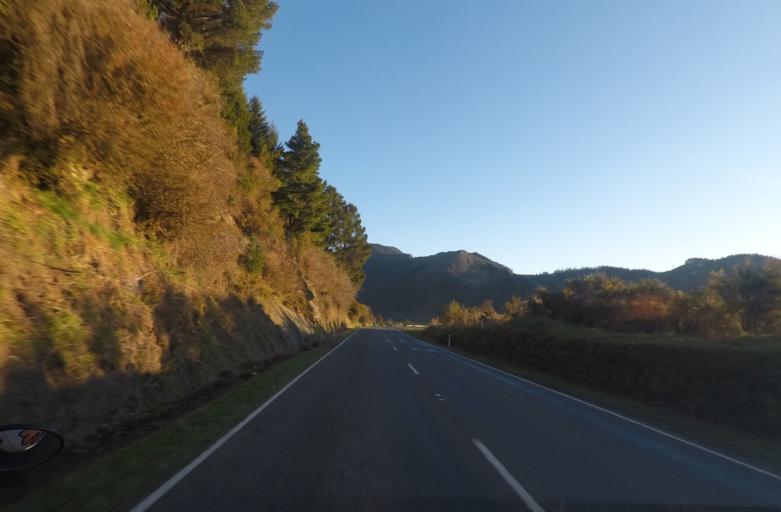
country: NZ
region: Marlborough
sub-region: Marlborough District
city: Picton
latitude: -41.2901
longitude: 173.6769
